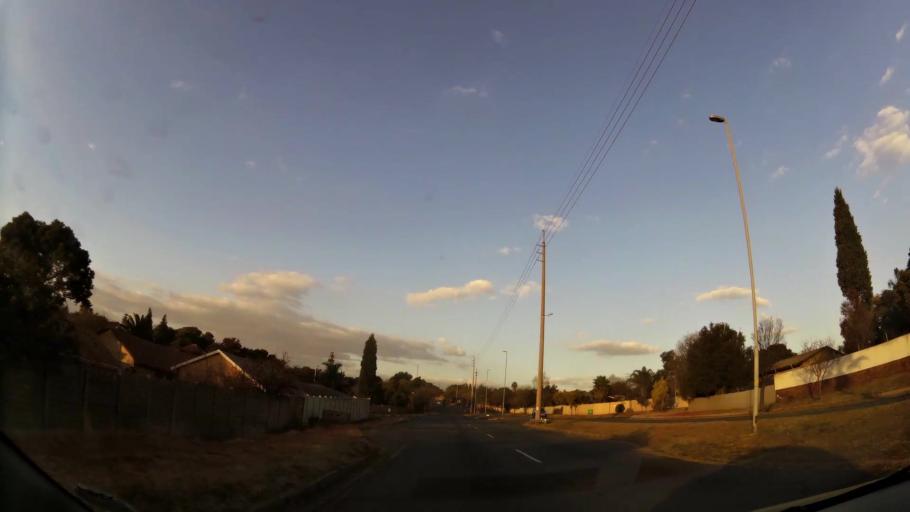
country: ZA
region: Gauteng
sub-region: West Rand District Municipality
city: Krugersdorp
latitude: -26.0791
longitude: 27.7734
